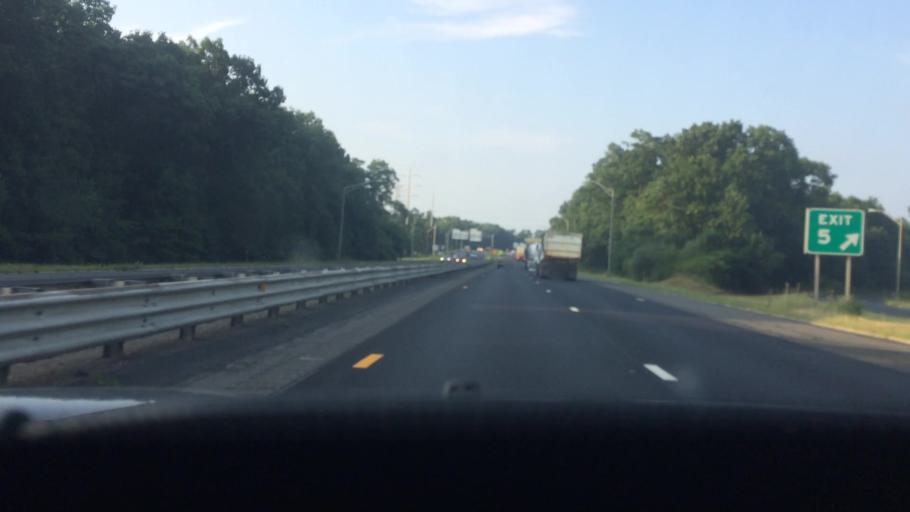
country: US
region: Massachusetts
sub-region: Hampden County
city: Chicopee
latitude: 42.1494
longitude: -72.5496
